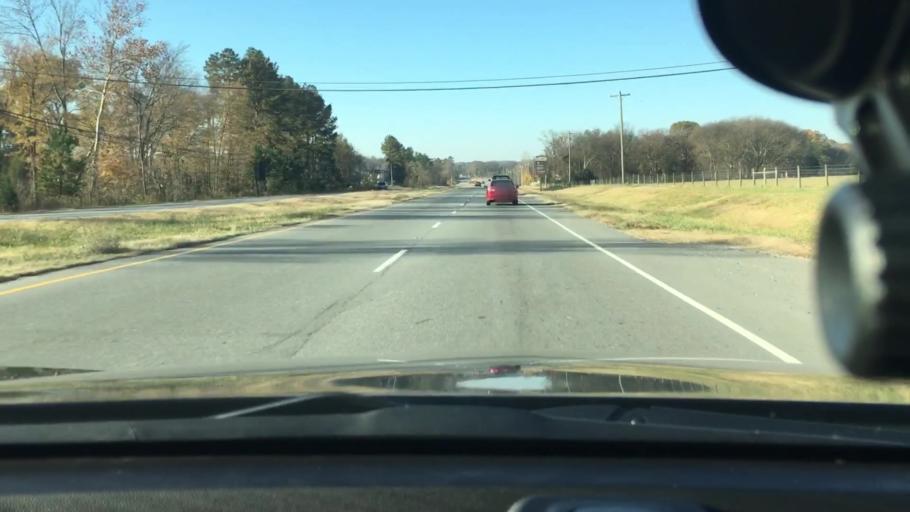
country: US
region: North Carolina
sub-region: Cabarrus County
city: Harrisburg
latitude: 35.3366
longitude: -80.6206
